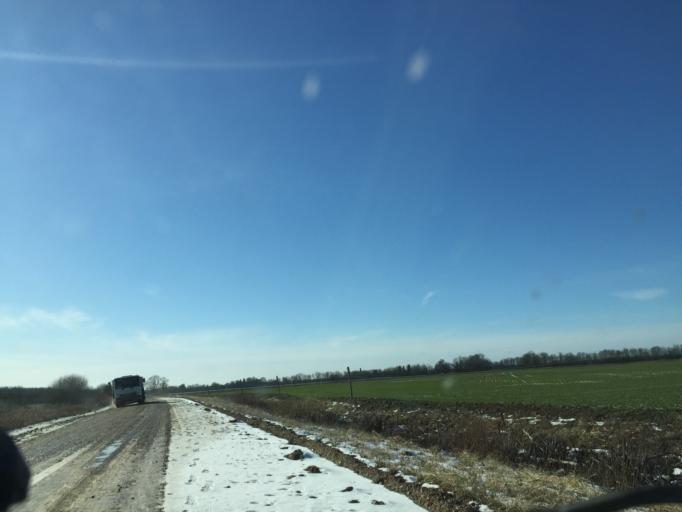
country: LV
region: Ventspils Rajons
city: Piltene
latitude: 57.2696
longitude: 21.6890
